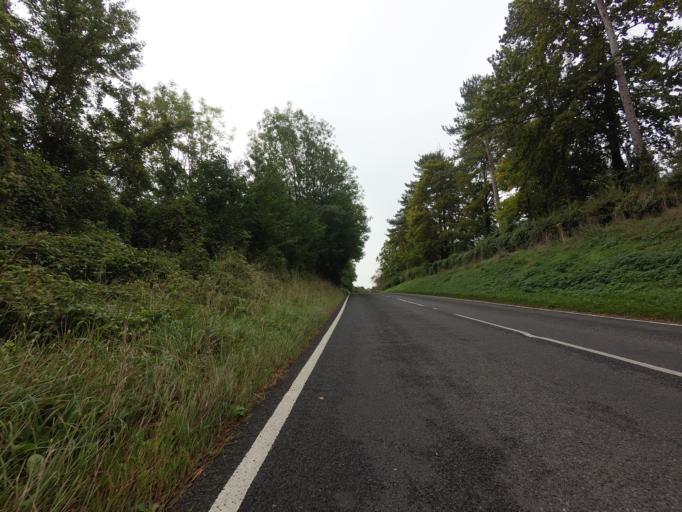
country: GB
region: England
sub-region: Hertfordshire
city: Reed
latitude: 52.0145
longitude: 0.0287
